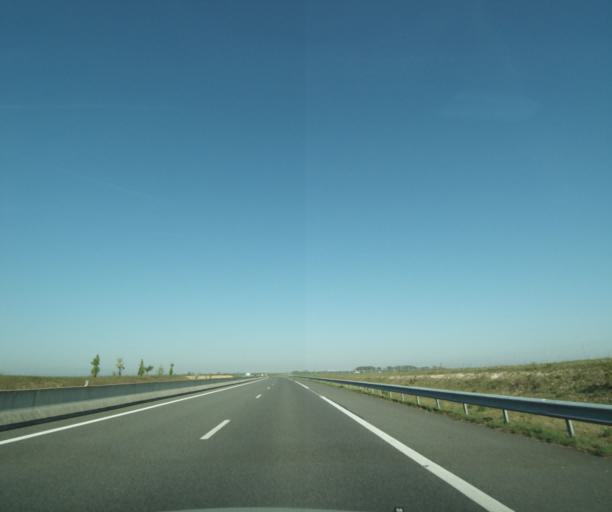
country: FR
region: Centre
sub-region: Departement du Loiret
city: Pannes
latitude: 48.0763
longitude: 2.6310
